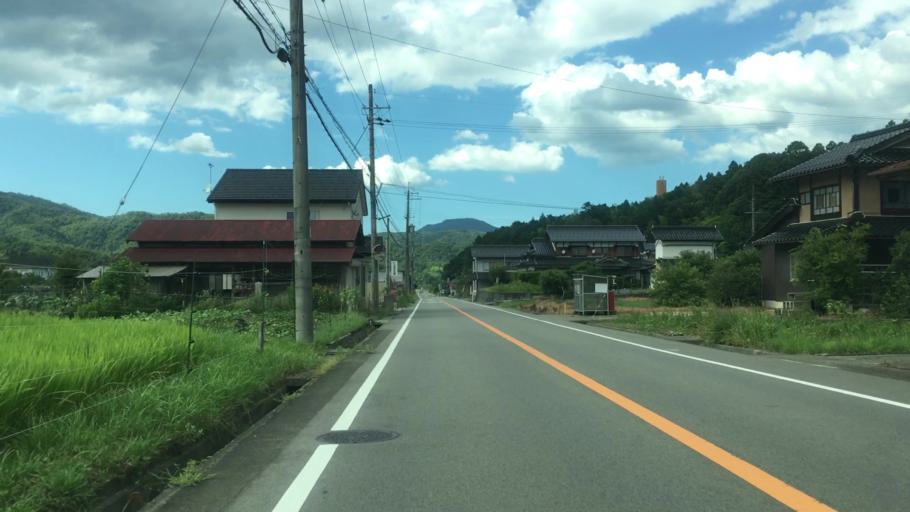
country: JP
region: Hyogo
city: Toyooka
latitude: 35.5413
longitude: 134.7902
